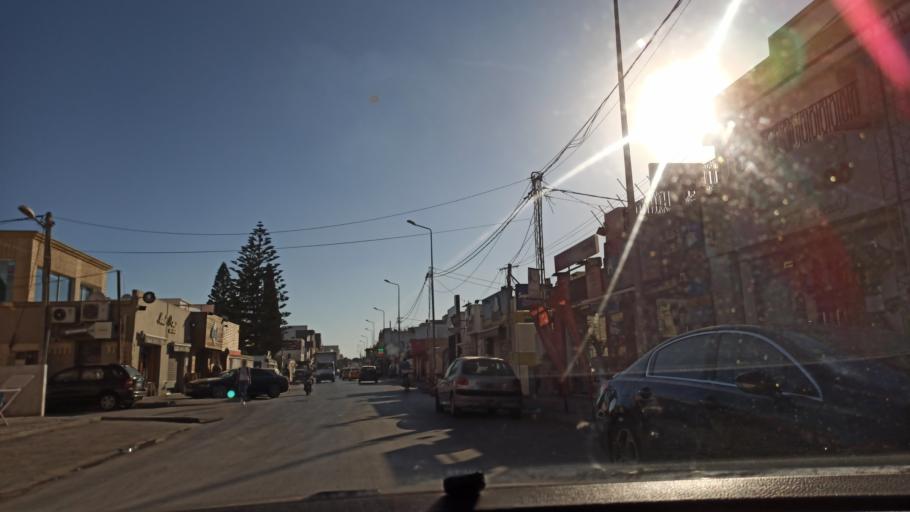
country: TN
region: Tunis
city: La Goulette
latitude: 36.8561
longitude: 10.2635
